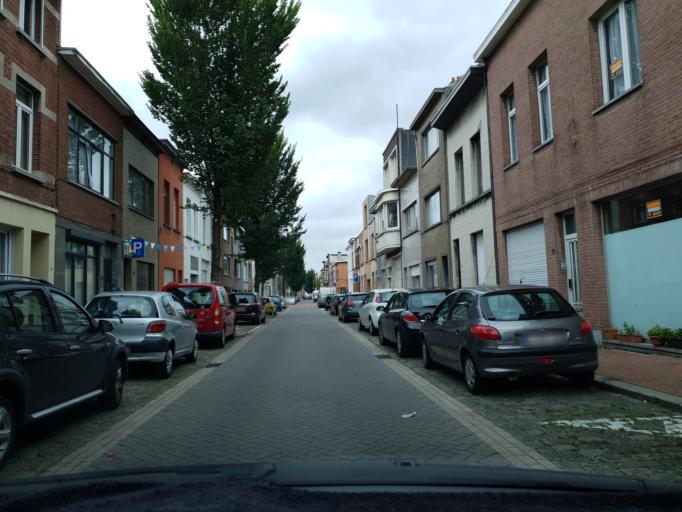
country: BE
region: Flanders
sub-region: Provincie Antwerpen
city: Borsbeek
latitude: 51.2238
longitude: 4.4614
